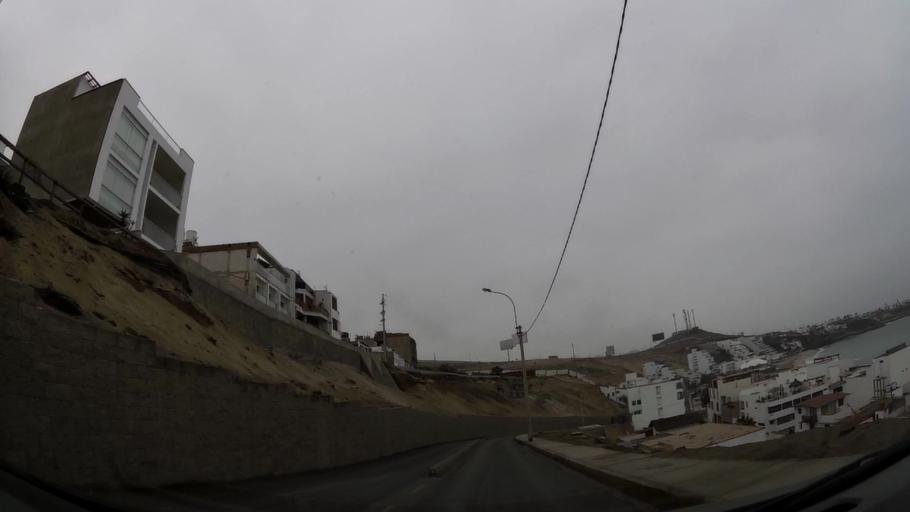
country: PE
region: Lima
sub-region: Lima
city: Punta Hermosa
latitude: -12.3382
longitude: -76.8197
